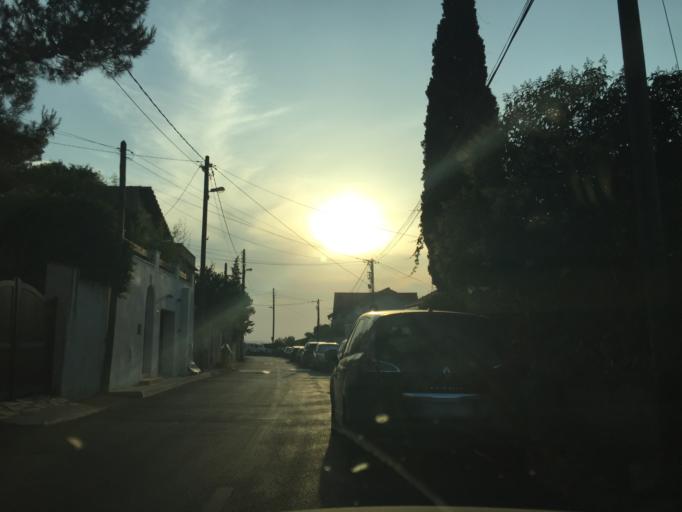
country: FR
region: Provence-Alpes-Cote d'Azur
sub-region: Departement des Bouches-du-Rhone
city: Marseille 09
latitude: 43.2444
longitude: 5.4193
